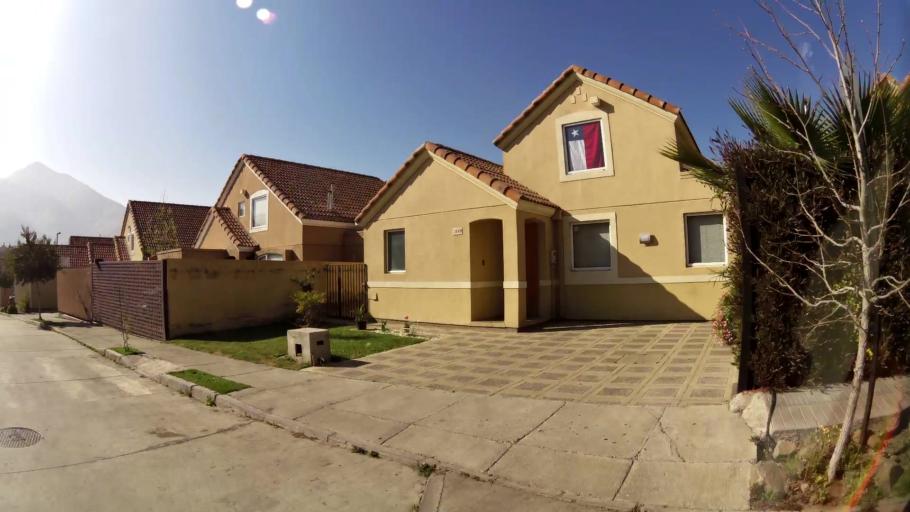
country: CL
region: Santiago Metropolitan
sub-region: Provincia de Chacabuco
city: Chicureo Abajo
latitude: -33.3448
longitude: -70.6772
